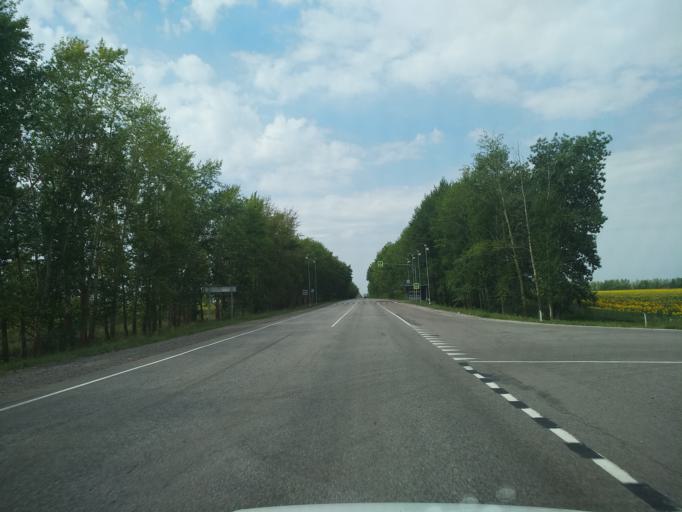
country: RU
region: Voronezj
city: Pereleshino
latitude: 51.7116
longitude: 40.0015
